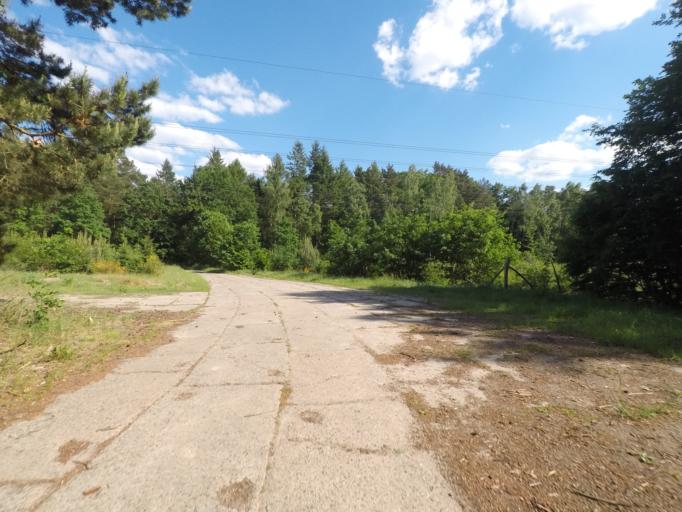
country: DE
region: Brandenburg
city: Britz
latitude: 52.8663
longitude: 13.7824
